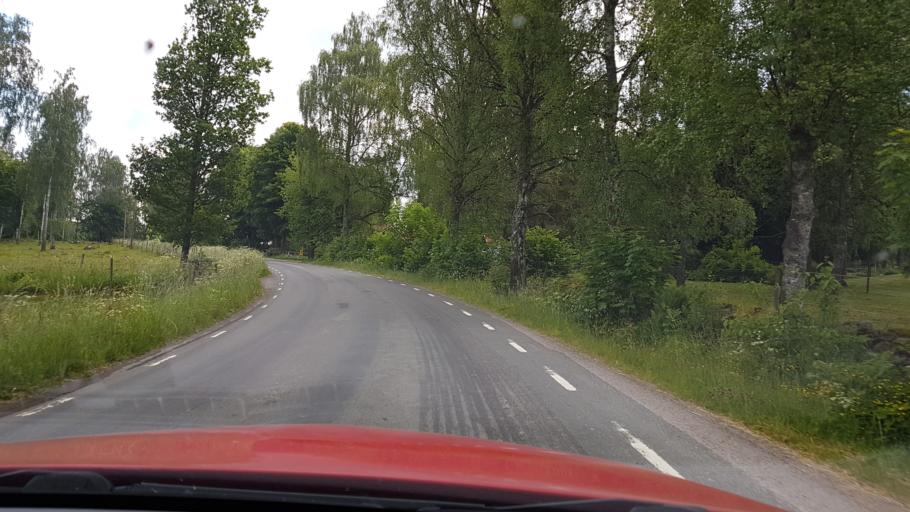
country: SE
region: Vaestra Goetaland
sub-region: Hjo Kommun
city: Hjo
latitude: 58.3112
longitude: 14.1786
